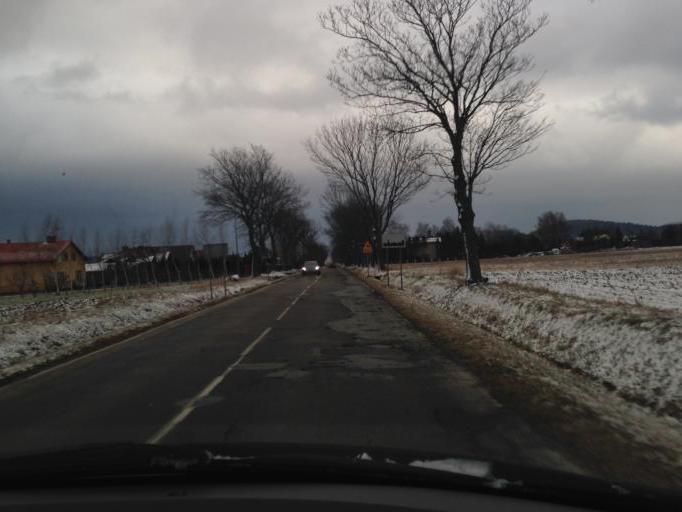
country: PL
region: Subcarpathian Voivodeship
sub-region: Powiat jasielski
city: Osiek Jasielski
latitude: 49.6117
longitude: 21.4611
